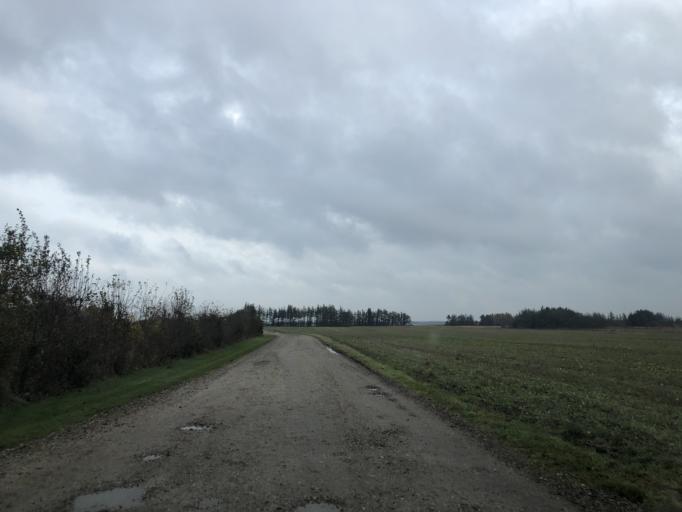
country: DK
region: Central Jutland
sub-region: Holstebro Kommune
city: Ulfborg
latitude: 56.3175
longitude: 8.2214
